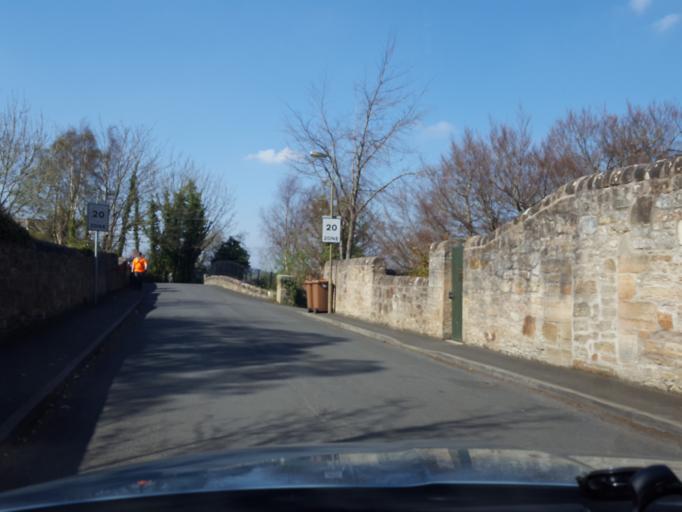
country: GB
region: Scotland
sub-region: West Lothian
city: Linlithgow
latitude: 55.9741
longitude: -3.6022
